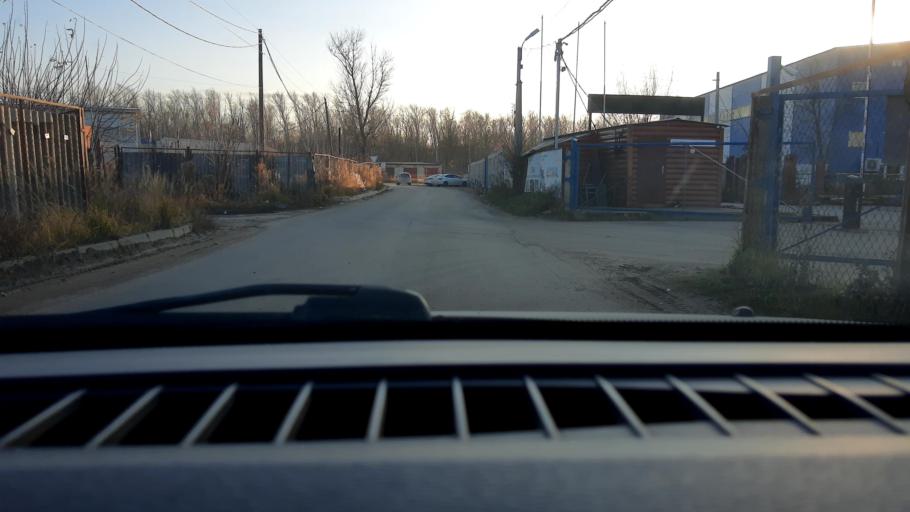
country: RU
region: Nizjnij Novgorod
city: Gorbatovka
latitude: 56.3167
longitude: 43.8559
